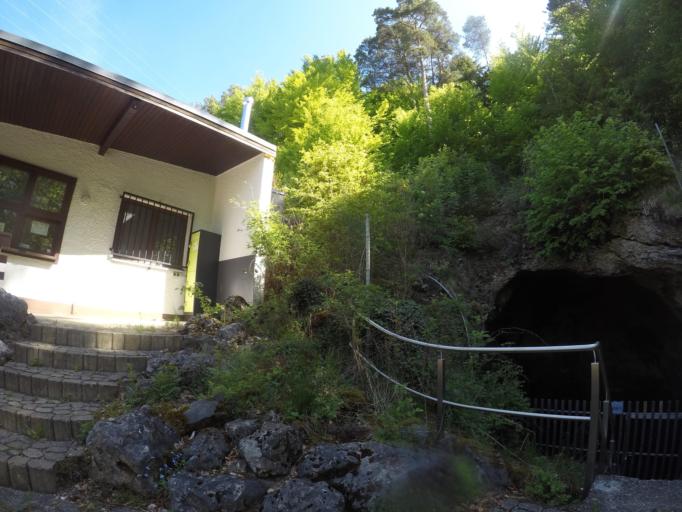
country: DE
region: Baden-Wuerttemberg
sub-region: Tuebingen Region
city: Laichingen
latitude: 48.4311
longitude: 9.6837
